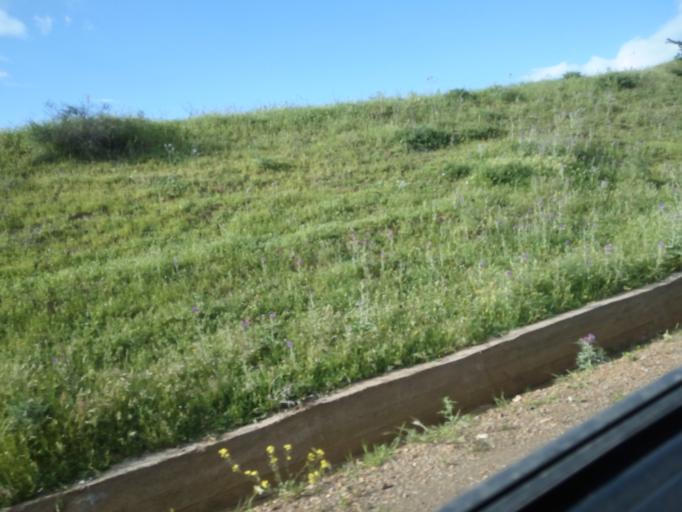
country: DZ
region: Tipaza
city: El Affroun
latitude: 36.3723
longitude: 2.5003
